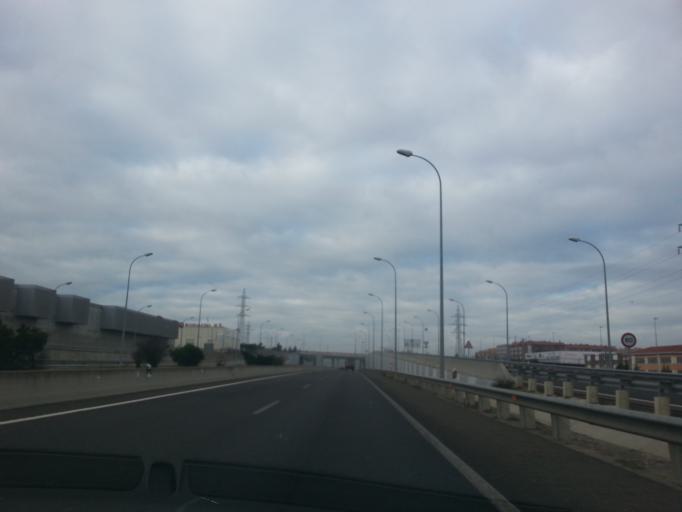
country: ES
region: Castille and Leon
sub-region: Provincia de Salamanca
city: Carbajosa de la Sagrada
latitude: 40.9417
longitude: -5.6647
